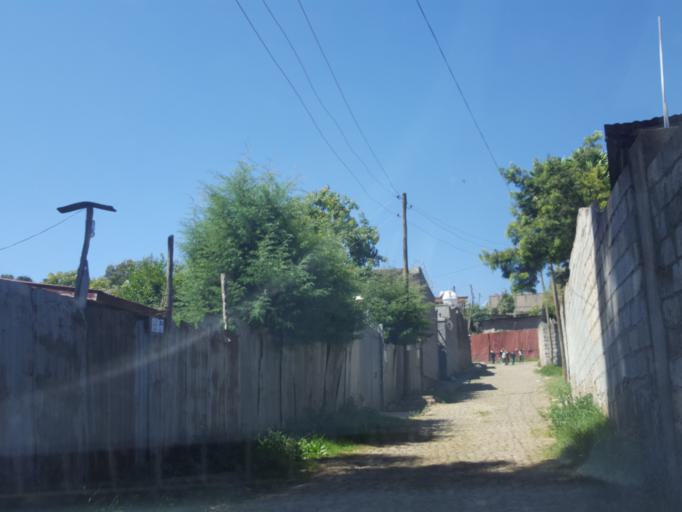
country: ET
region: Adis Abeba
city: Addis Ababa
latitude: 9.0591
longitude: 38.7463
